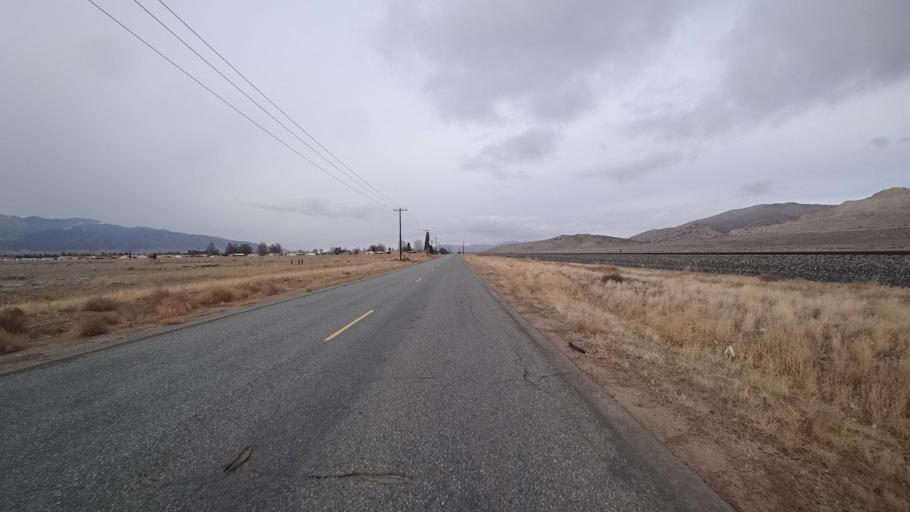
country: US
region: California
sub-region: Kern County
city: Tehachapi
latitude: 35.1236
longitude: -118.3849
